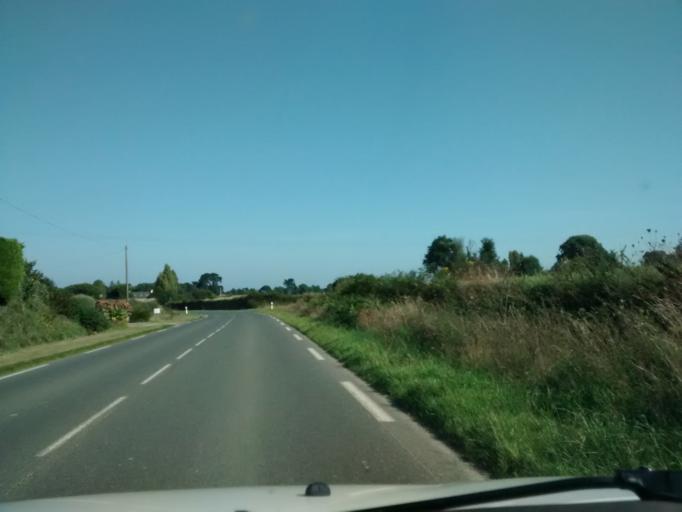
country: FR
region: Brittany
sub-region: Departement des Cotes-d'Armor
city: Tredarzec
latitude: 48.7993
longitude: -3.2001
